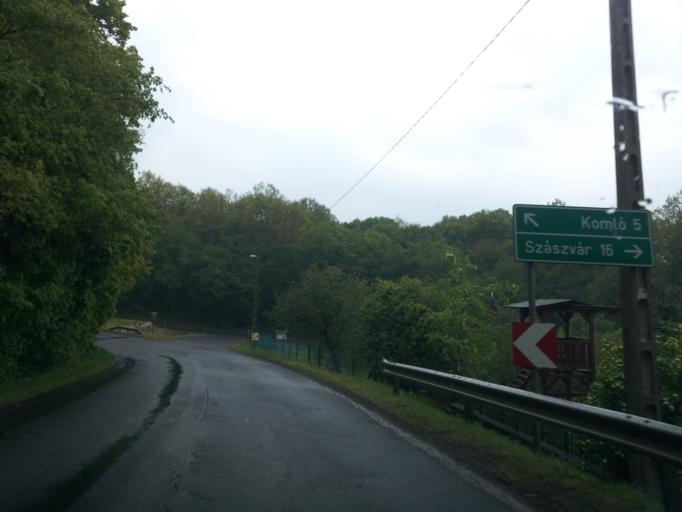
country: HU
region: Baranya
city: Hosszuheteny
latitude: 46.1853
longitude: 18.3190
